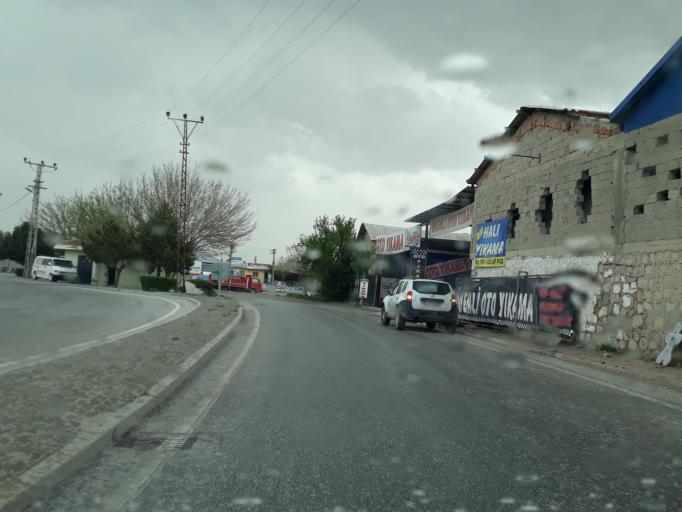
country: TR
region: Konya
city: Selcuklu
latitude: 37.9166
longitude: 32.4758
